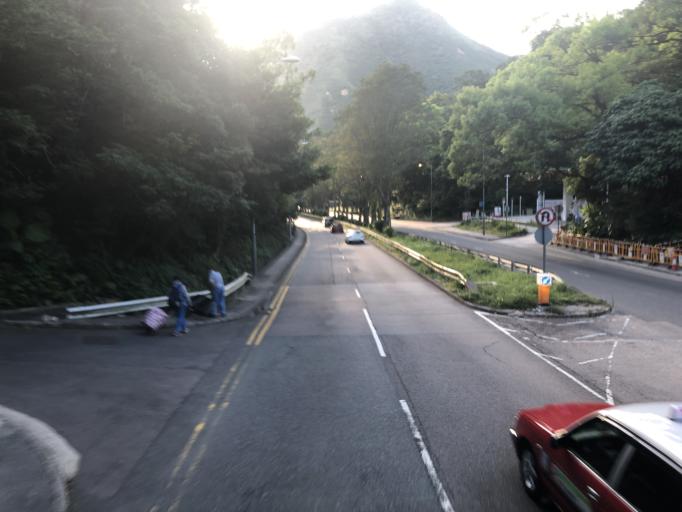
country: HK
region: Wong Tai Sin
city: Wong Tai Sin
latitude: 22.3334
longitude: 114.2335
